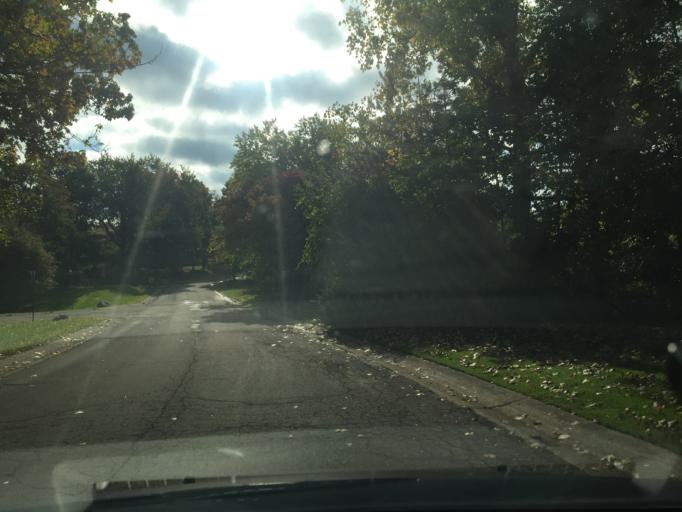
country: US
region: Michigan
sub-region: Oakland County
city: Sylvan Lake
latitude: 42.5876
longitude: -83.3114
